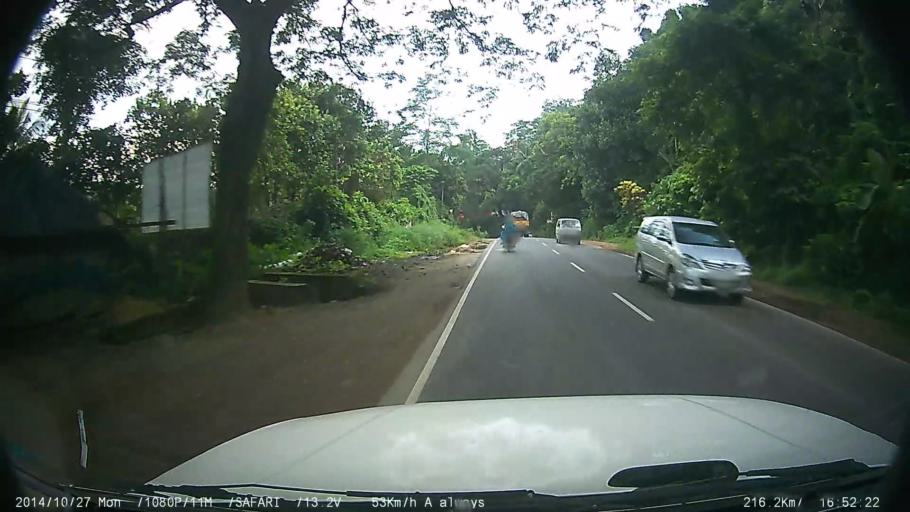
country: IN
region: Kerala
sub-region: Thrissur District
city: Chelakara
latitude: 10.5742
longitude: 76.3847
